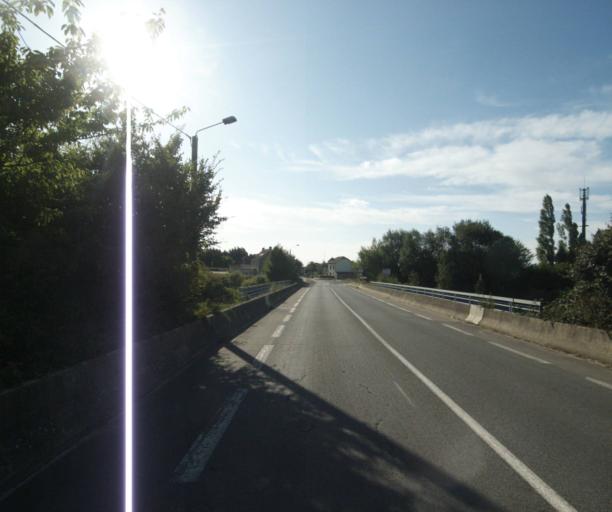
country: FR
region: Nord-Pas-de-Calais
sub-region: Departement du Nord
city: Cysoing
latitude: 50.5750
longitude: 3.1998
